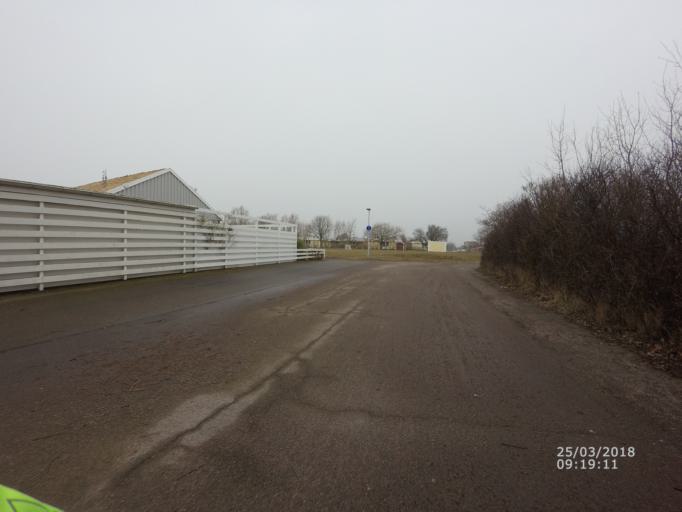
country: SE
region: Skane
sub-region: Hoganas Kommun
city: Hoganas
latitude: 56.1525
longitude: 12.5798
